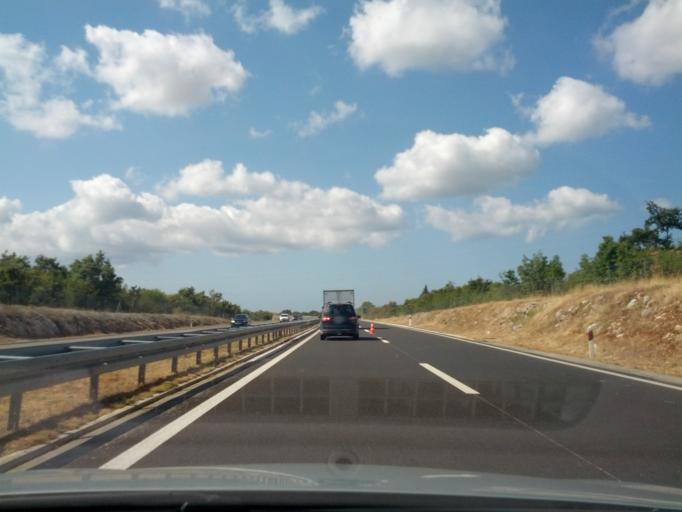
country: HR
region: Istarska
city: Vodnjan
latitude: 45.0154
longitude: 13.8407
